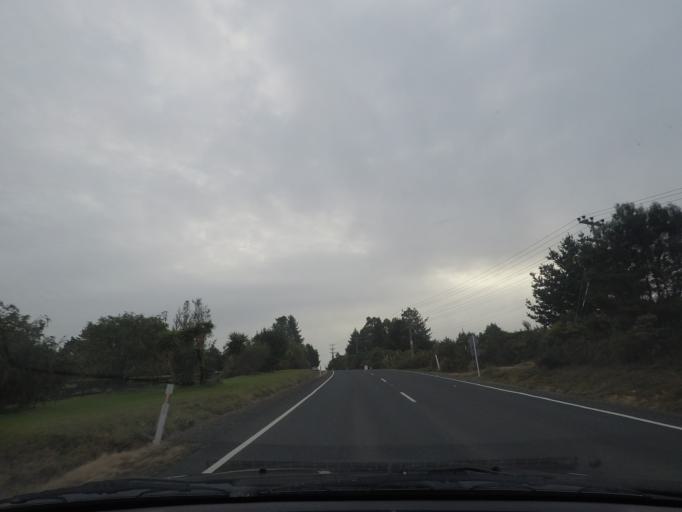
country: NZ
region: Auckland
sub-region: Auckland
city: Muriwai Beach
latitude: -36.7612
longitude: 174.5703
